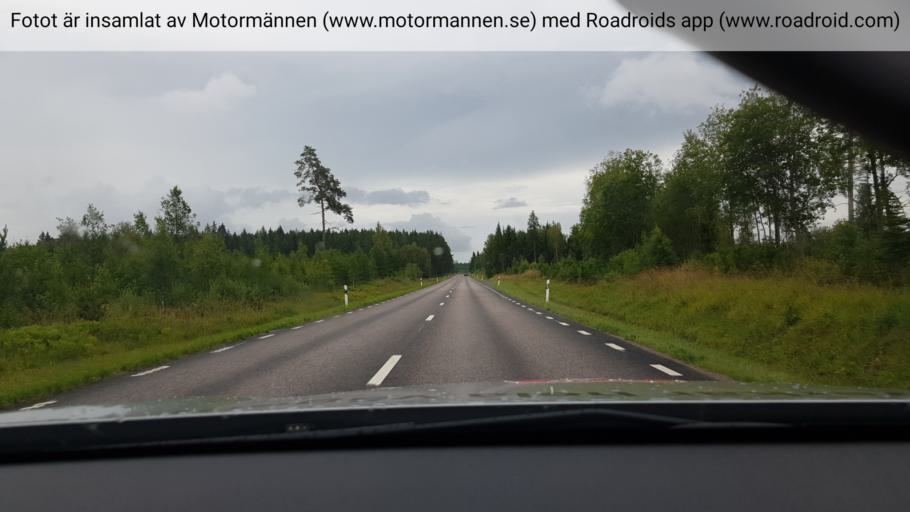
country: SE
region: Uppsala
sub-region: Tierps Kommun
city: Karlholmsbruk
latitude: 60.5382
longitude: 17.5632
